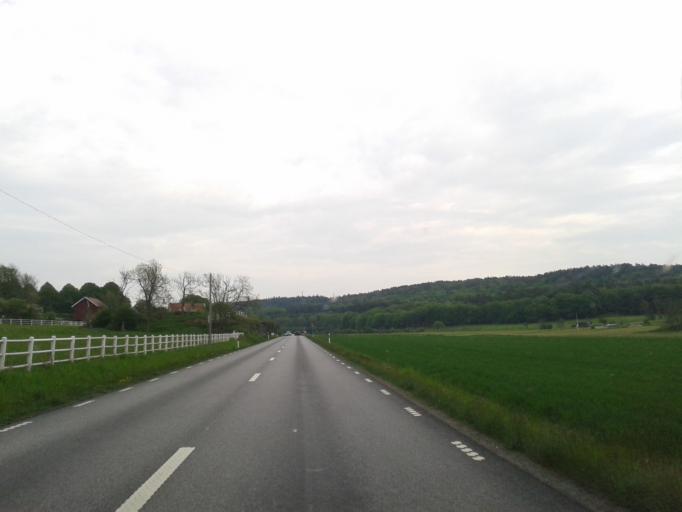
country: SE
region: Vaestra Goetaland
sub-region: Kungalvs Kommun
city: Kode
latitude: 57.8906
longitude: 11.7699
